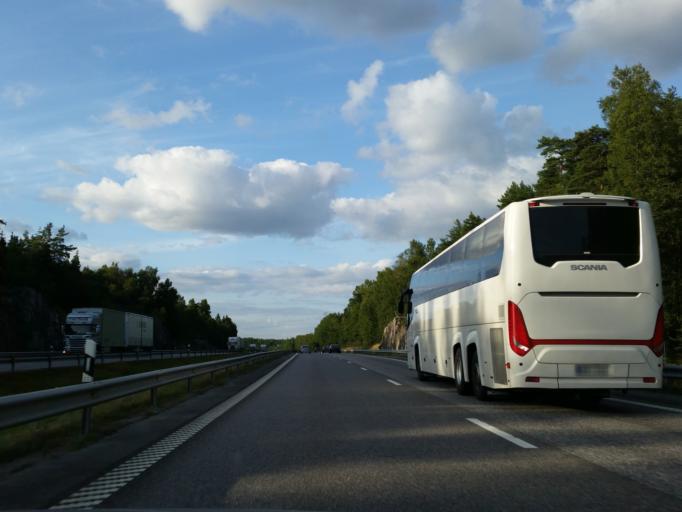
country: SE
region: Stockholm
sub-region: Sodertalje Kommun
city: Pershagen
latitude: 59.0967
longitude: 17.6051
